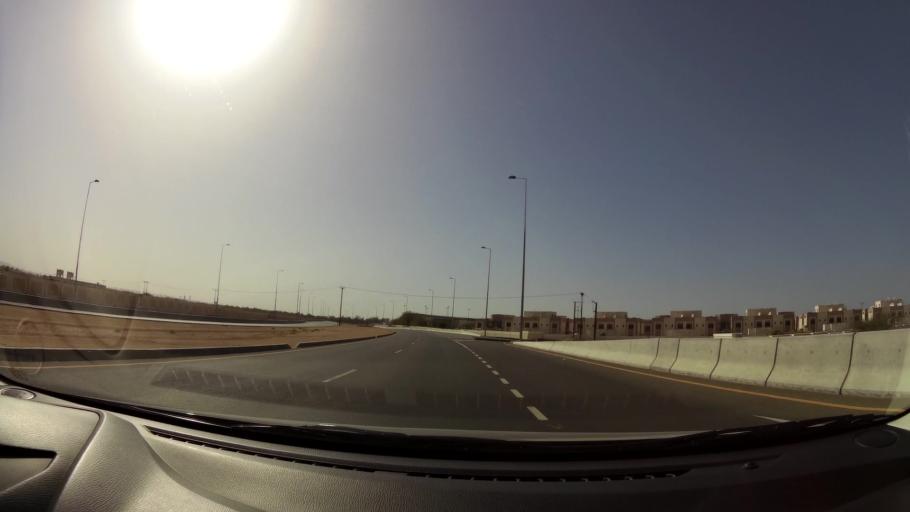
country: OM
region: Muhafazat Masqat
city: Bawshar
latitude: 23.5779
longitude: 58.2761
